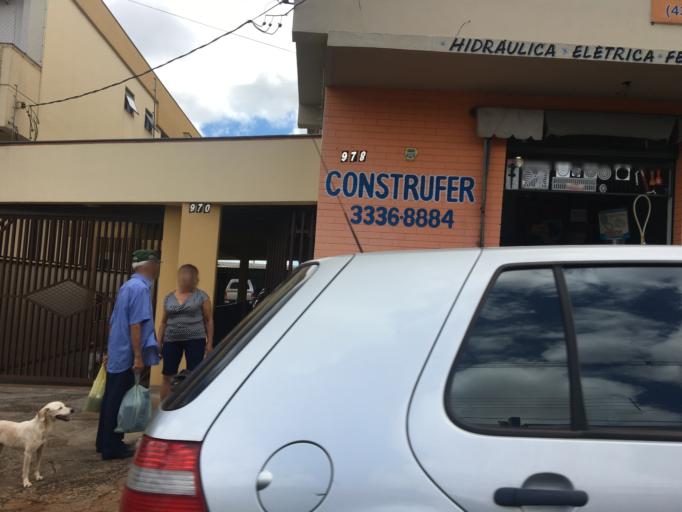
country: BR
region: Parana
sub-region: Londrina
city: Londrina
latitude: -23.2988
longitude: -51.1628
